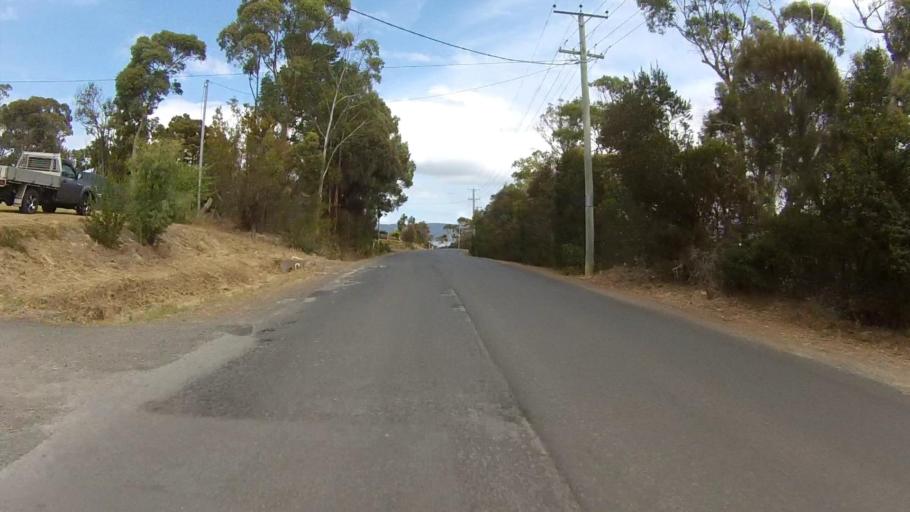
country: AU
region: Tasmania
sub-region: Kingborough
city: Margate
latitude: -43.0233
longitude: 147.2912
